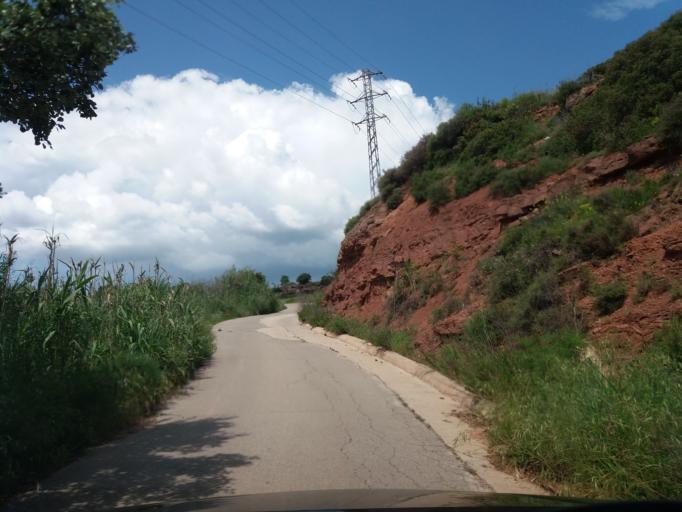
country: ES
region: Catalonia
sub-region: Provincia de Barcelona
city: Sant Joan de Vilatorrada
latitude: 41.7433
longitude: 1.7963
